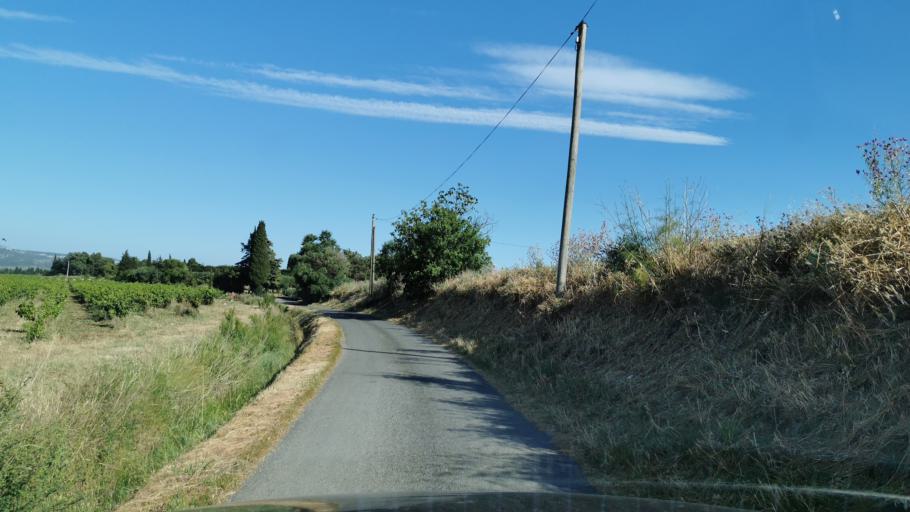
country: FR
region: Languedoc-Roussillon
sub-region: Departement de l'Aude
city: Narbonne
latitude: 43.1606
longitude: 3.0001
